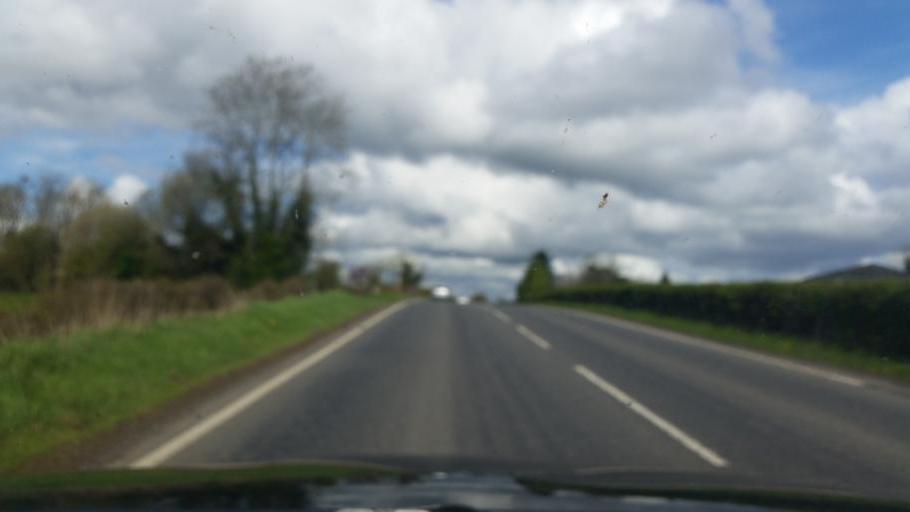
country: IE
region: Ulster
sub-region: An Cabhan
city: Ballyconnell
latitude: 54.1466
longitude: -7.5177
